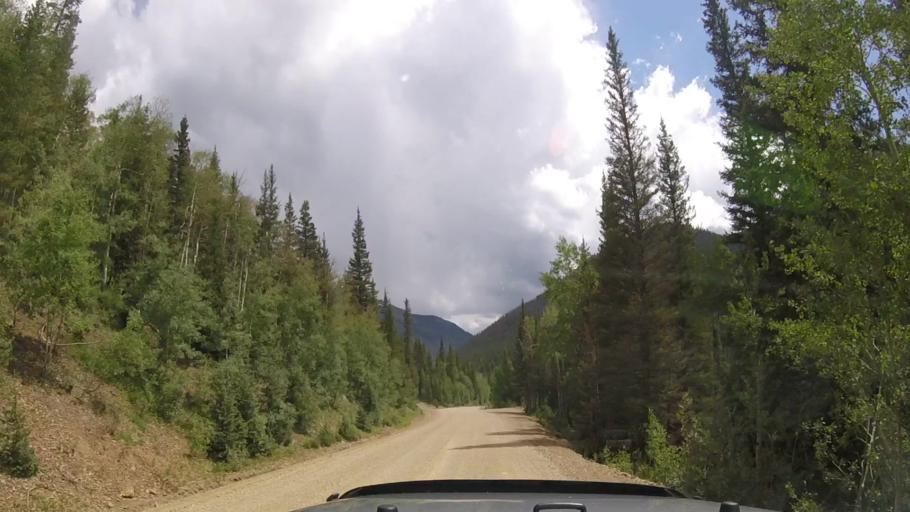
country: US
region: Colorado
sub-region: San Juan County
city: Silverton
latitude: 37.8314
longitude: -107.6711
